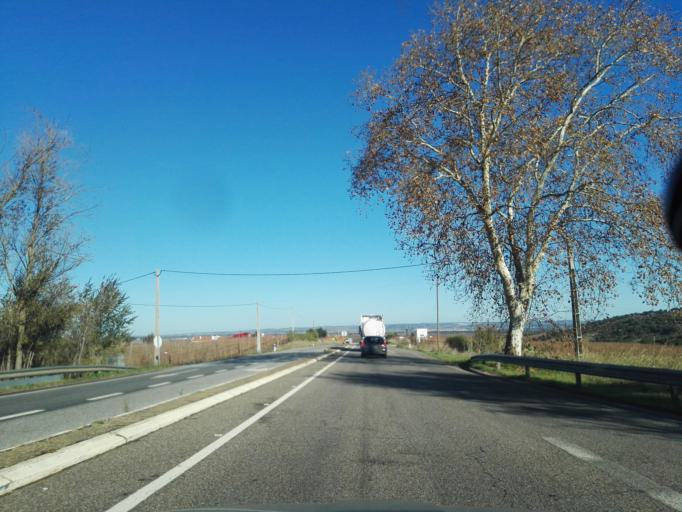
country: PT
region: Evora
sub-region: Borba
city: Borba
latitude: 38.8141
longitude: -7.4483
